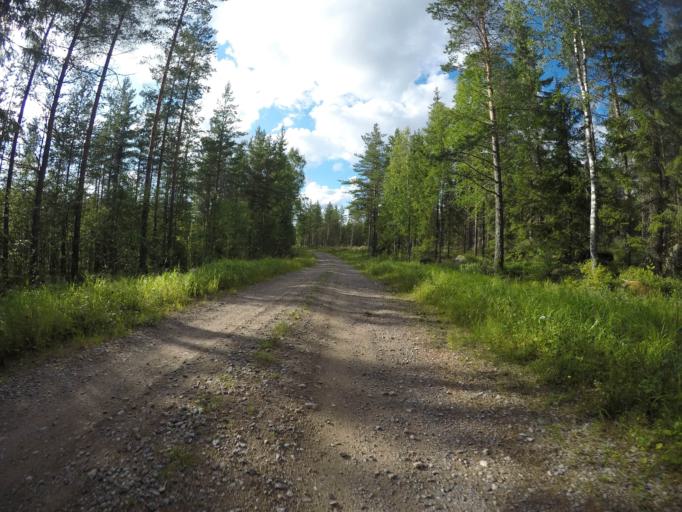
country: SE
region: OErebro
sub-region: Hallefors Kommun
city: Haellefors
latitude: 59.9583
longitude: 14.5646
